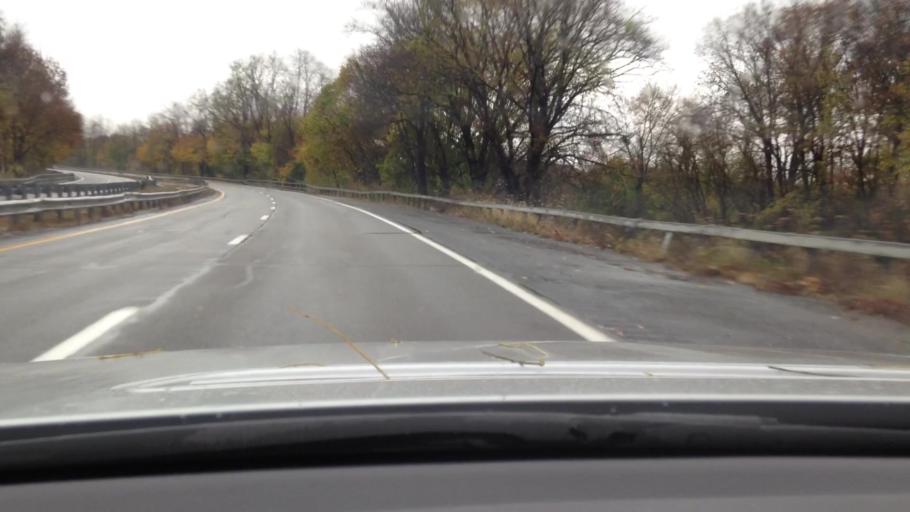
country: US
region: New York
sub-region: Westchester County
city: Buchanan
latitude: 41.2717
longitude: -73.9340
